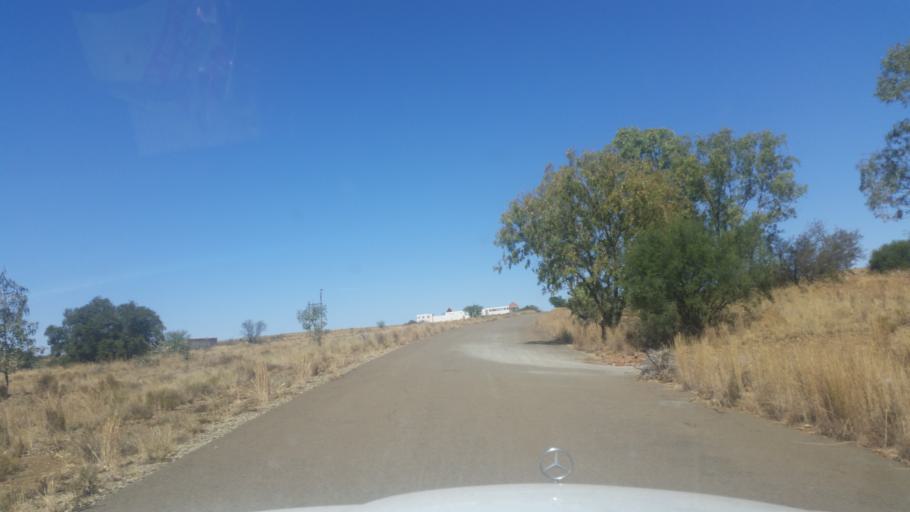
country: ZA
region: Eastern Cape
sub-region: Joe Gqabi District Municipality
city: Burgersdorp
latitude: -30.6926
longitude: 25.7798
